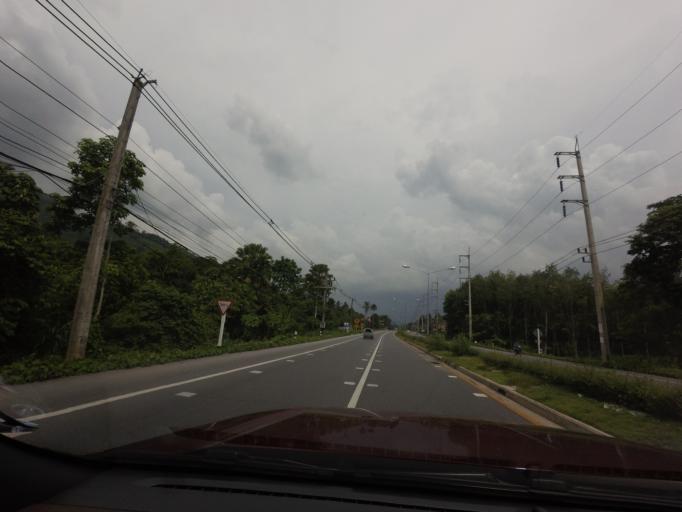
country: TH
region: Yala
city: Yala
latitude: 6.4830
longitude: 101.2655
